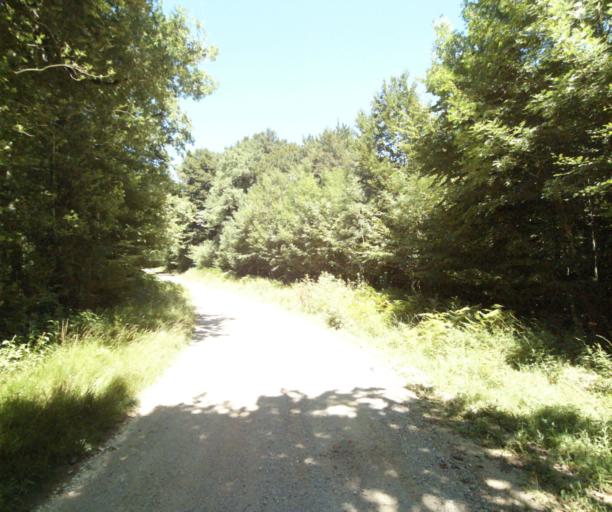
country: FR
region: Midi-Pyrenees
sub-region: Departement du Tarn
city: Dourgne
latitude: 43.4214
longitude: 2.1526
